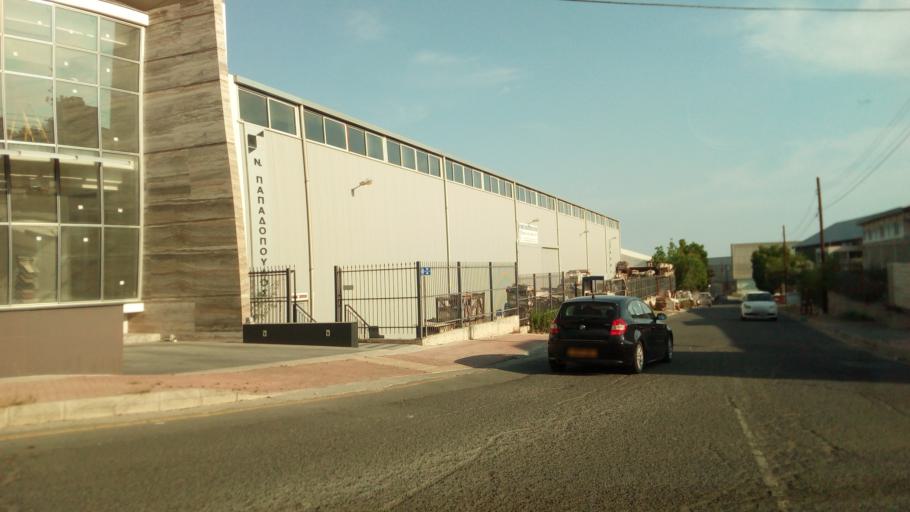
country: CY
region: Limassol
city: Limassol
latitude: 34.7047
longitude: 33.0664
